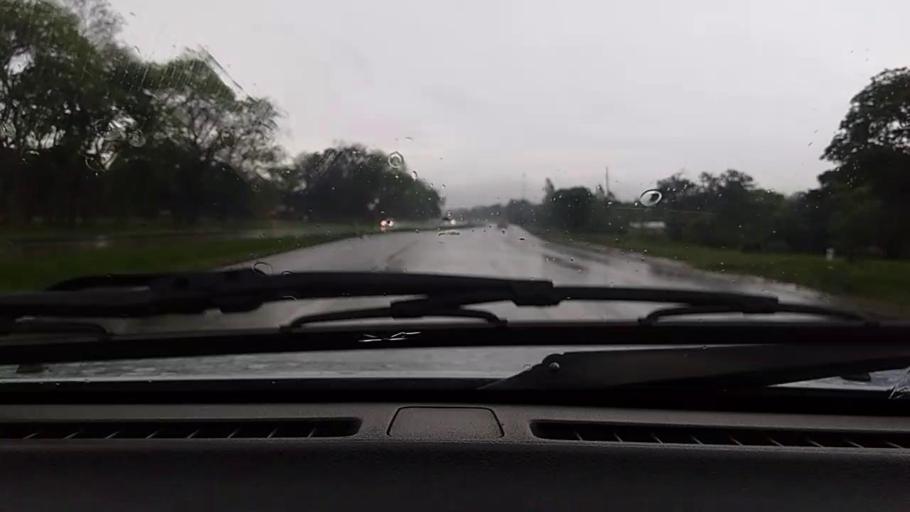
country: PY
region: Caaguazu
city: Repatriacion
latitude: -25.4549
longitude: -55.9120
